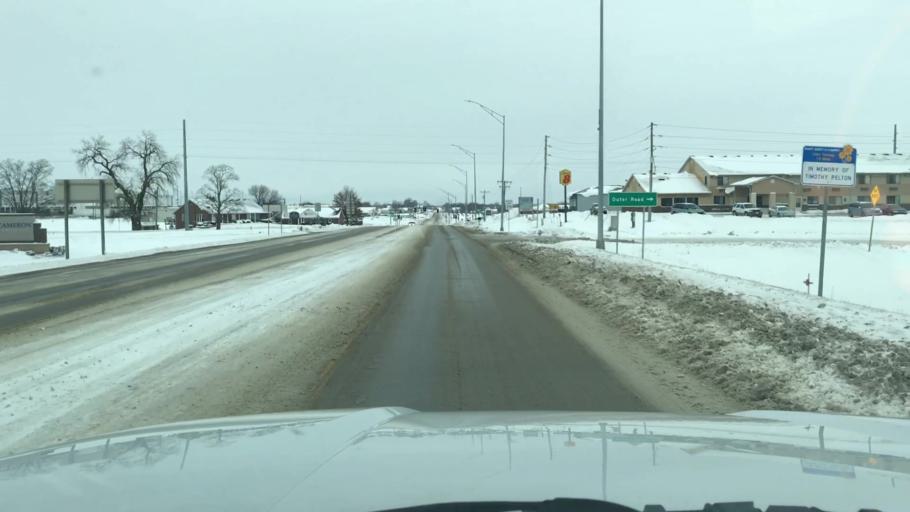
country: US
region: Missouri
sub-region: Clinton County
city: Cameron
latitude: 39.7555
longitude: -94.2343
